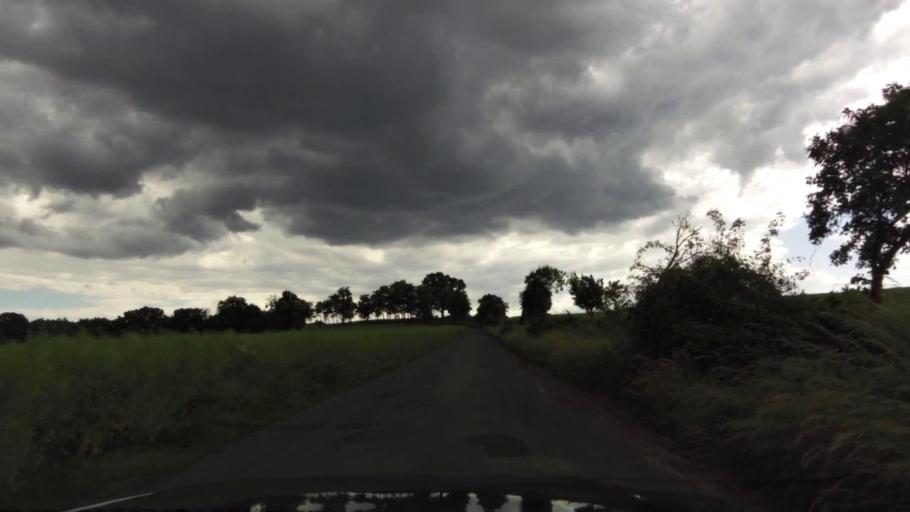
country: PL
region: West Pomeranian Voivodeship
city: Trzcinsko Zdroj
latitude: 52.9260
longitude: 14.5927
